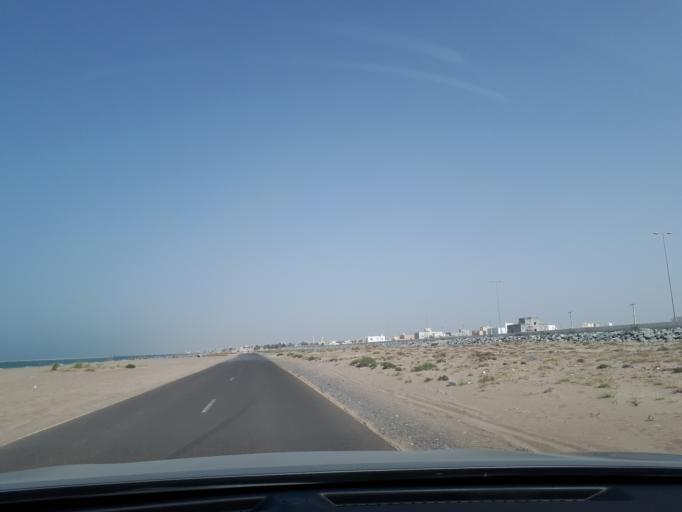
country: OM
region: Al Batinah
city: Barka'
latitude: 23.7144
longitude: 57.8706
